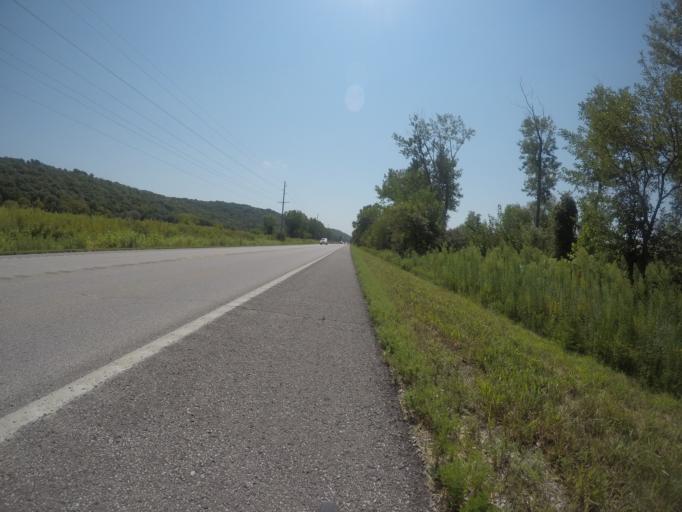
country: US
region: Kansas
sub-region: Atchison County
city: Atchison
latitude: 39.5037
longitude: -95.0093
